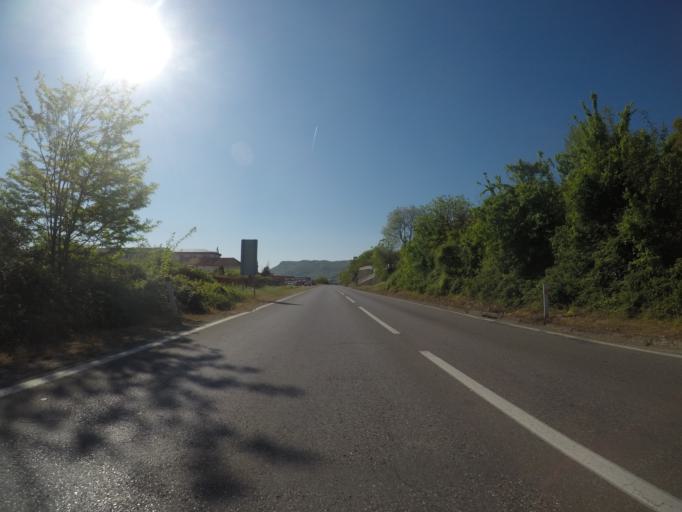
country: ME
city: Spuz
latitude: 42.4767
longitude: 19.1708
